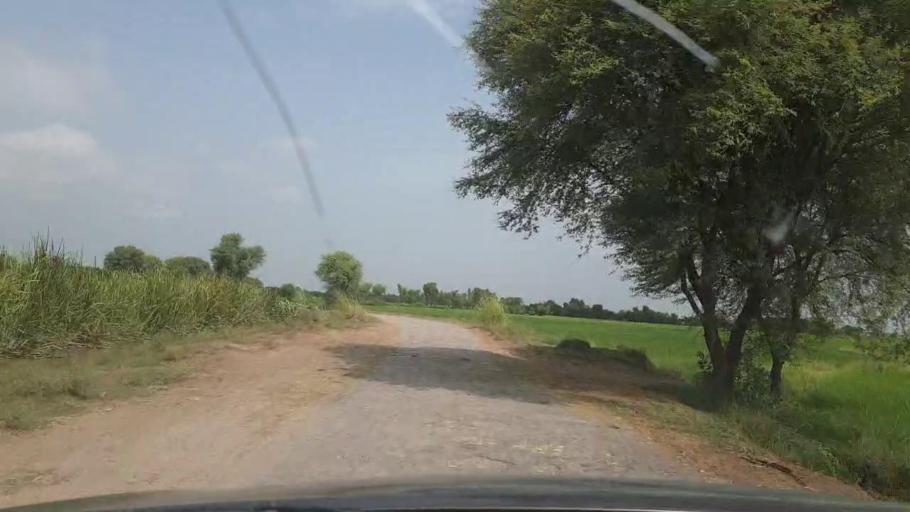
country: PK
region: Sindh
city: Ratodero
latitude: 27.8493
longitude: 68.3021
